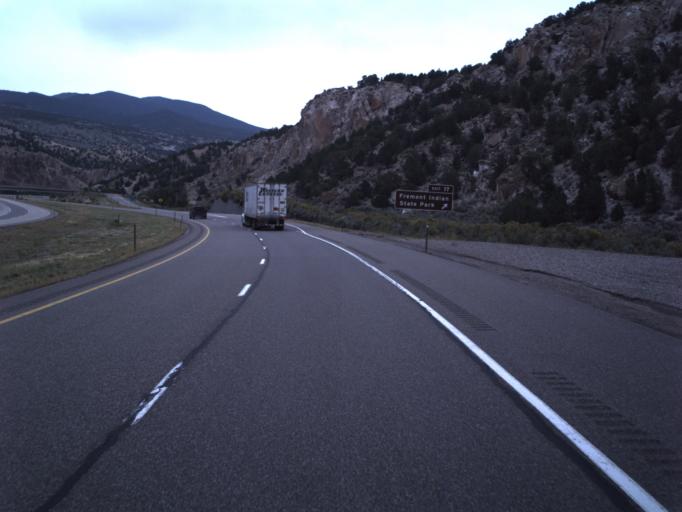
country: US
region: Utah
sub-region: Sevier County
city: Monroe
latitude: 38.5661
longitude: -112.3537
